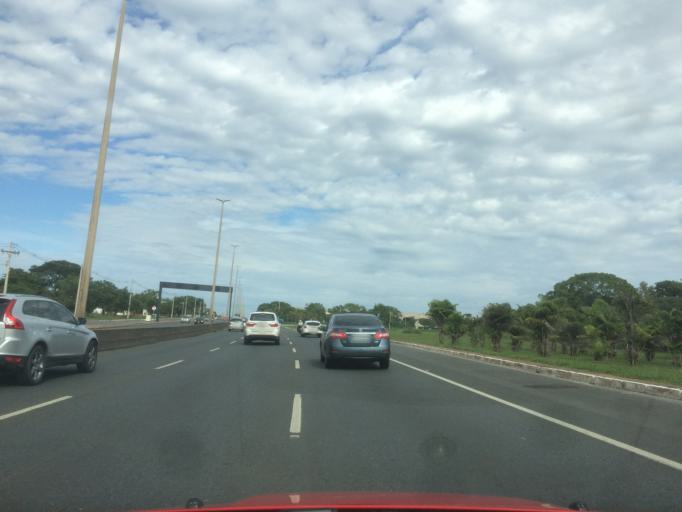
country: BR
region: Federal District
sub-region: Brasilia
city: Brasilia
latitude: -15.8173
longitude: -47.8346
